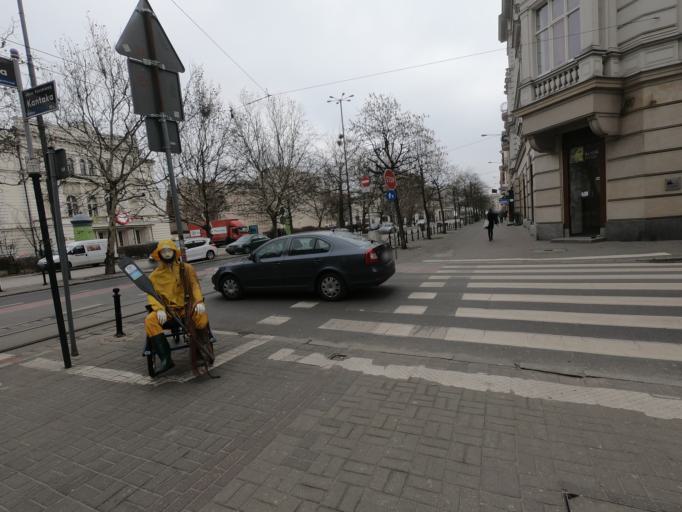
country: PL
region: Greater Poland Voivodeship
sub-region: Poznan
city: Poznan
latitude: 52.4082
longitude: 16.9231
